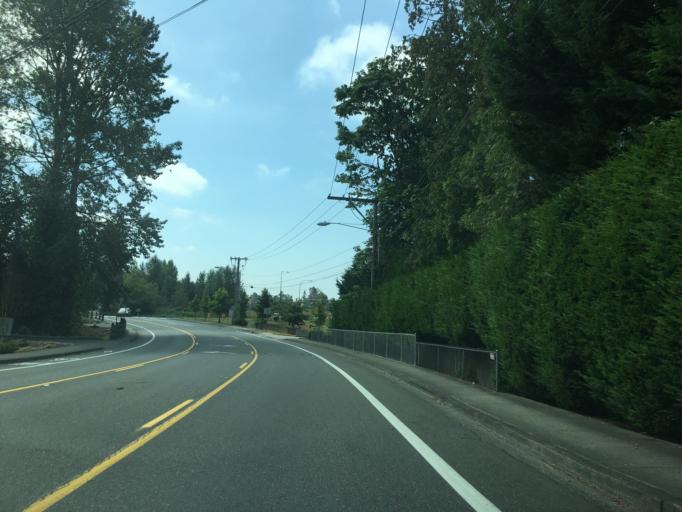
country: US
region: Washington
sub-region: King County
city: Kingsgate
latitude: 47.7450
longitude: -122.1848
